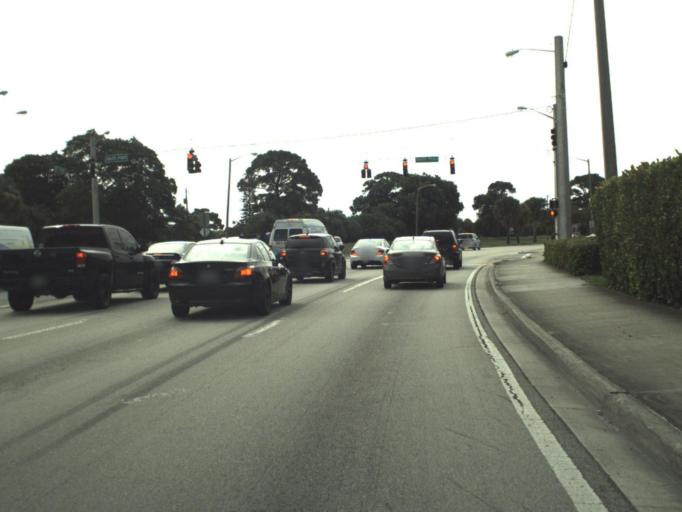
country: US
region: Florida
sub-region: Palm Beach County
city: Mangonia Park
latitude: 26.7579
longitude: -80.0829
